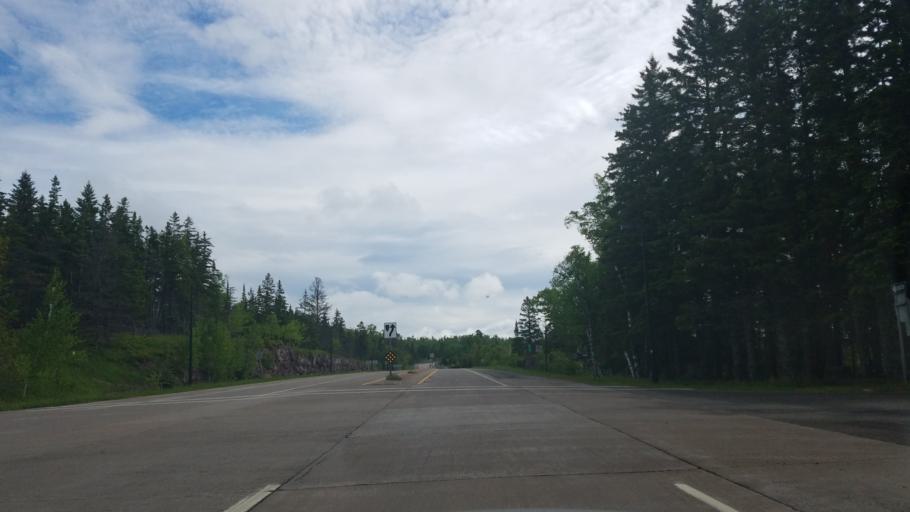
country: US
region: Minnesota
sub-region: Lake County
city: Two Harbors
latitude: 47.1392
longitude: -91.4740
